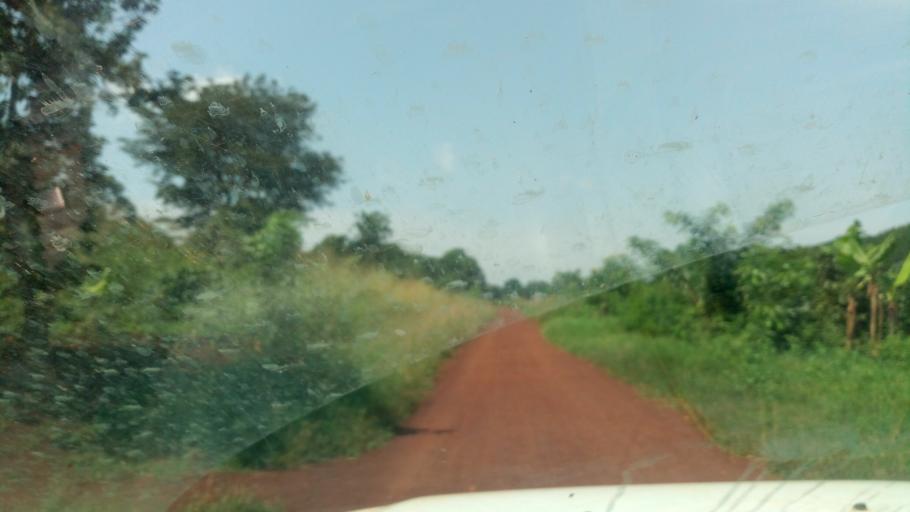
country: UG
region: Western Region
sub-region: Masindi District
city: Masindi
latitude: 1.6453
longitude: 31.8052
